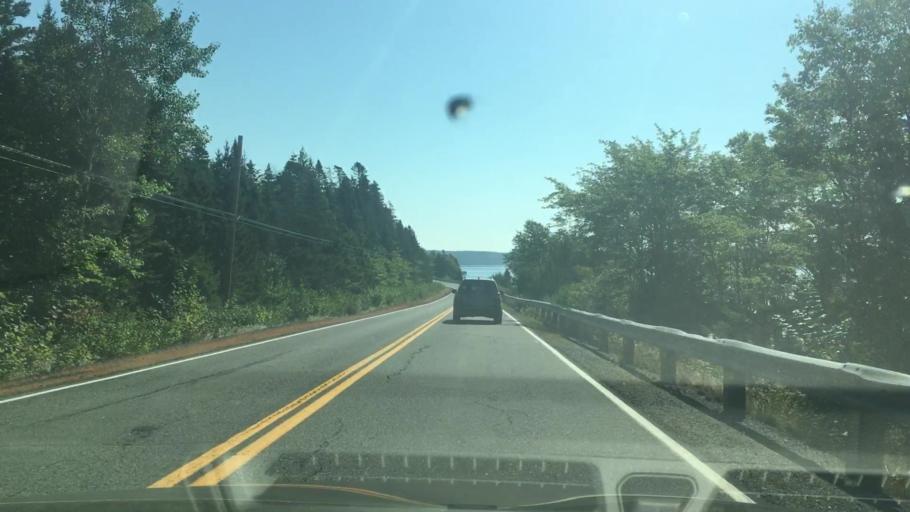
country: CA
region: Nova Scotia
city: Cole Harbour
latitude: 44.8151
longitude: -62.8766
